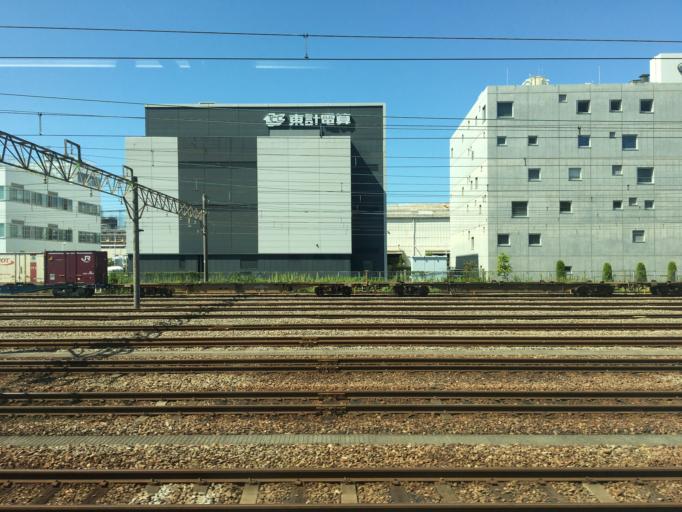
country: JP
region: Kanagawa
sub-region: Kawasaki-shi
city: Kawasaki
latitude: 35.5572
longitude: 139.6690
